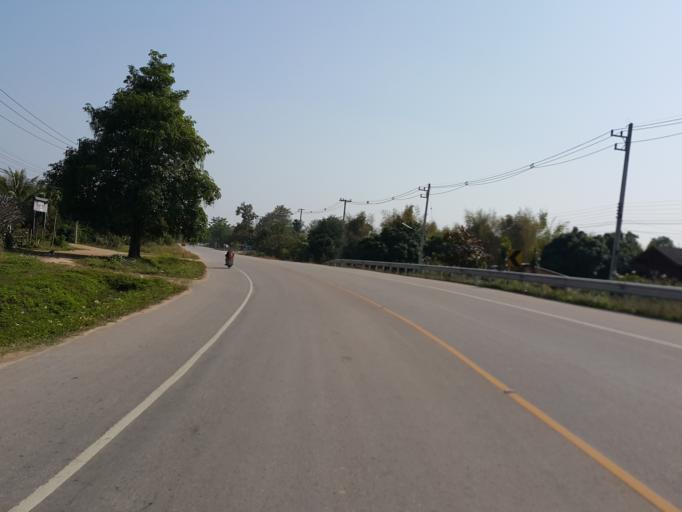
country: TH
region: Lampang
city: Chae Hom
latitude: 18.7520
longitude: 99.5721
